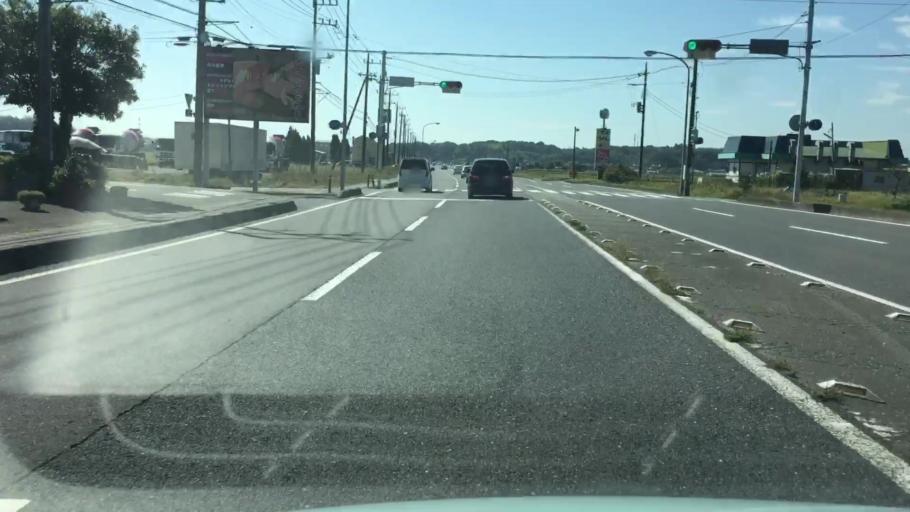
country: JP
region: Ibaraki
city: Ryugasaki
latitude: 35.8916
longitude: 140.1624
